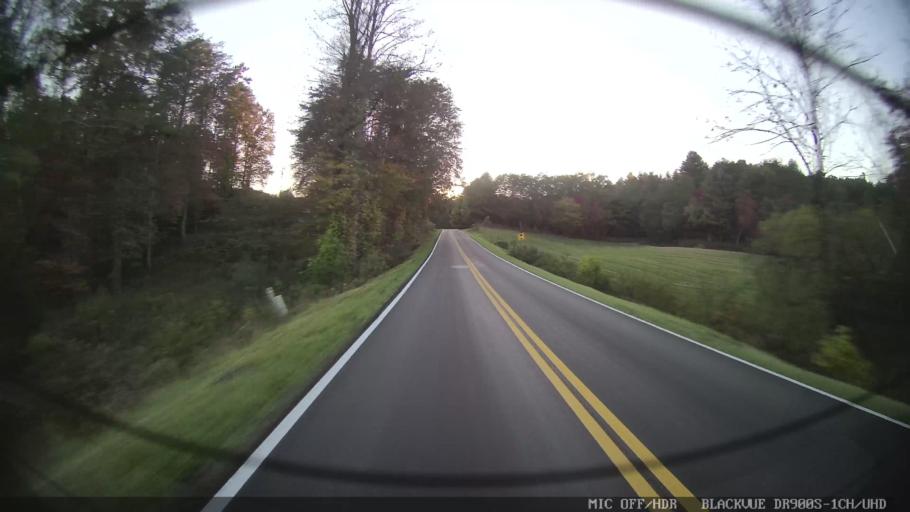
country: US
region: Georgia
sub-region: Union County
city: Blairsville
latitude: 34.8529
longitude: -83.9137
